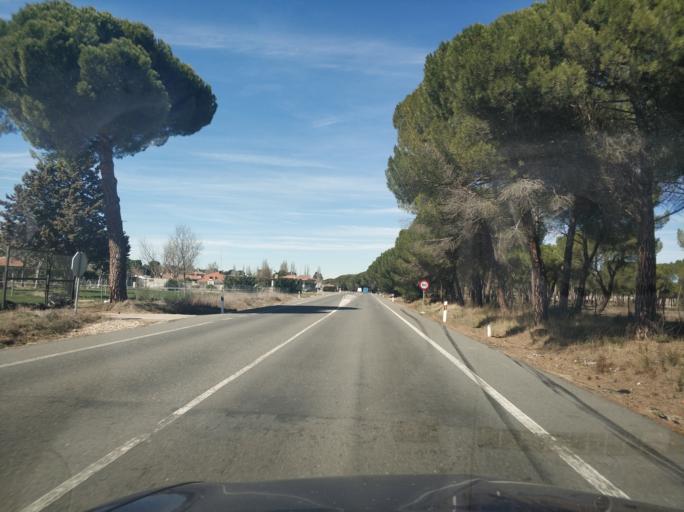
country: ES
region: Castille and Leon
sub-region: Provincia de Valladolid
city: Viana de Cega
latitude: 41.5406
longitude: -4.7748
